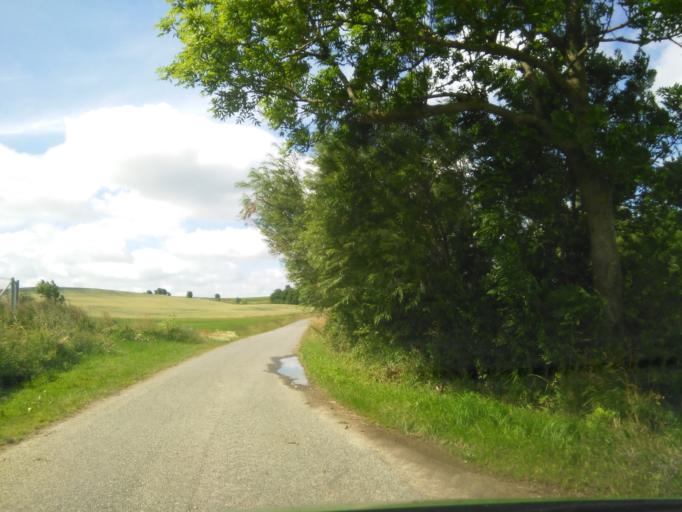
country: DK
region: Central Jutland
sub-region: Syddjurs Kommune
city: Ronde
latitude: 56.2410
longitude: 10.4866
